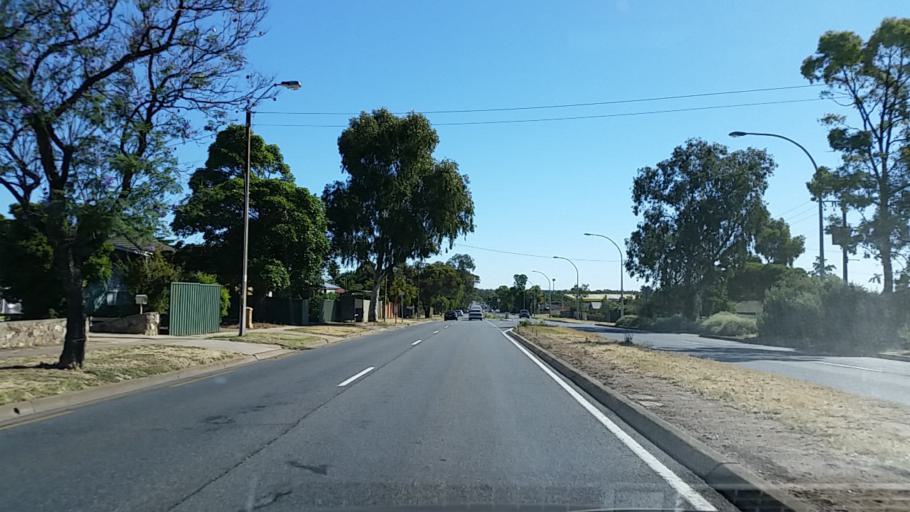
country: AU
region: South Australia
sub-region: Salisbury
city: Ingle Farm
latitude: -34.8018
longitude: 138.6537
